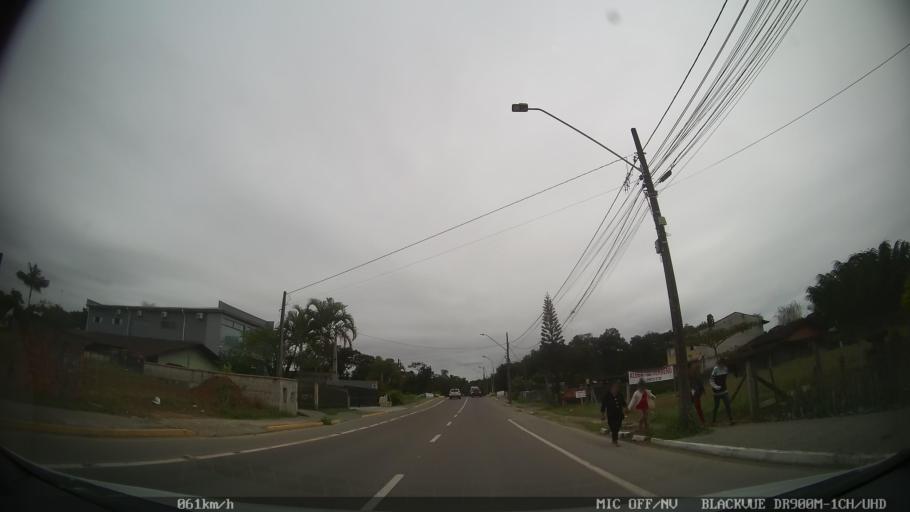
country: BR
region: Santa Catarina
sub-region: Joinville
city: Joinville
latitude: -26.2921
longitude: -48.8971
